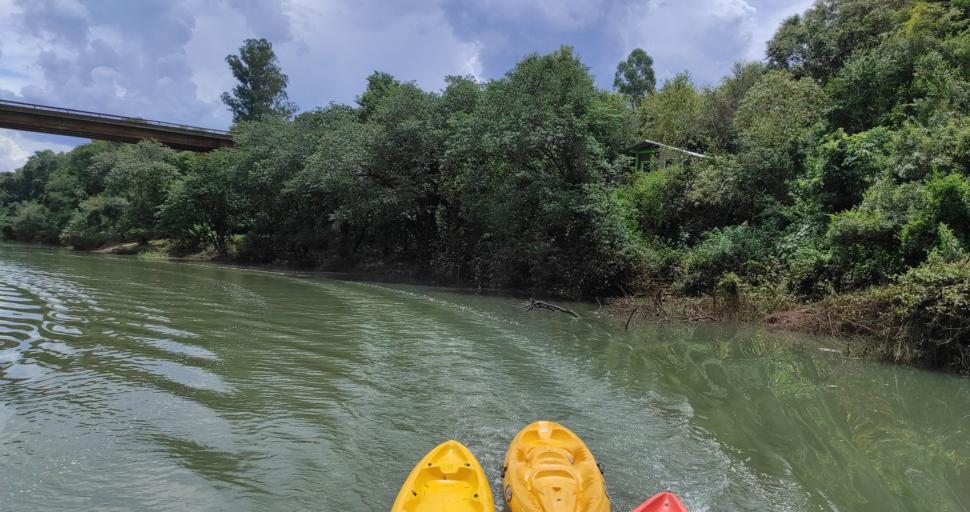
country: AR
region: Misiones
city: El Soberbio
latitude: -27.2801
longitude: -54.1956
